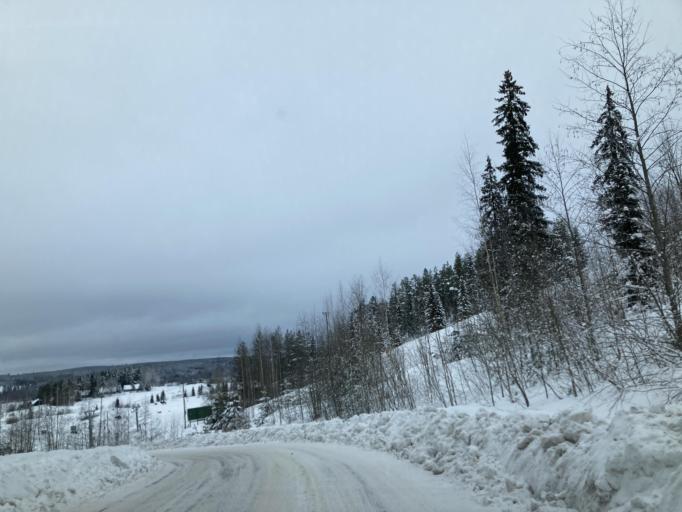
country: FI
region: Central Finland
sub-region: Jaemsae
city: Jaemsae
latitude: 61.8797
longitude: 25.3066
